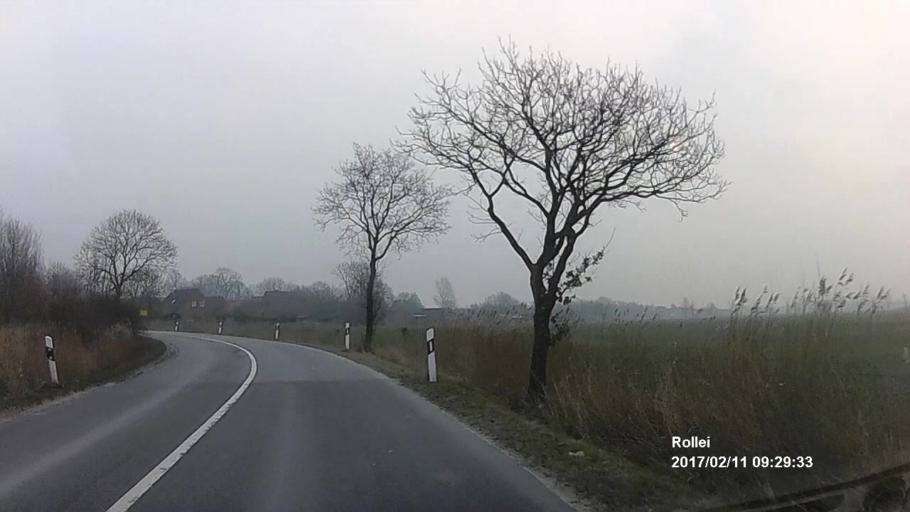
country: DE
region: Lower Saxony
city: Hinte
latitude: 53.4381
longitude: 7.1660
